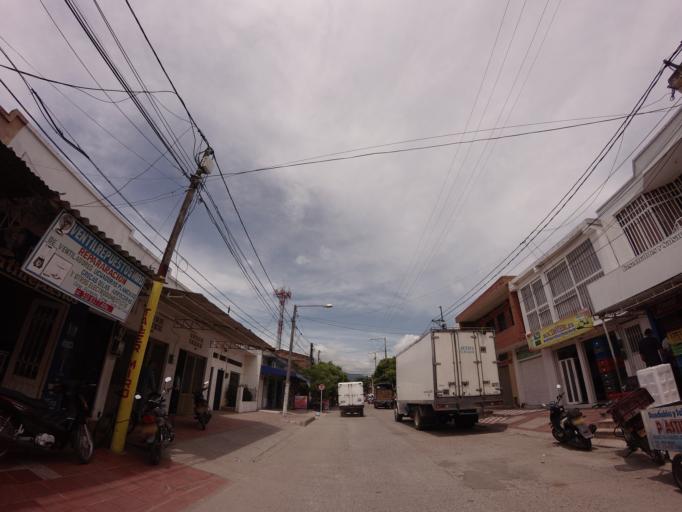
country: CO
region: Caldas
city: La Dorada
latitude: 5.4536
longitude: -74.6662
